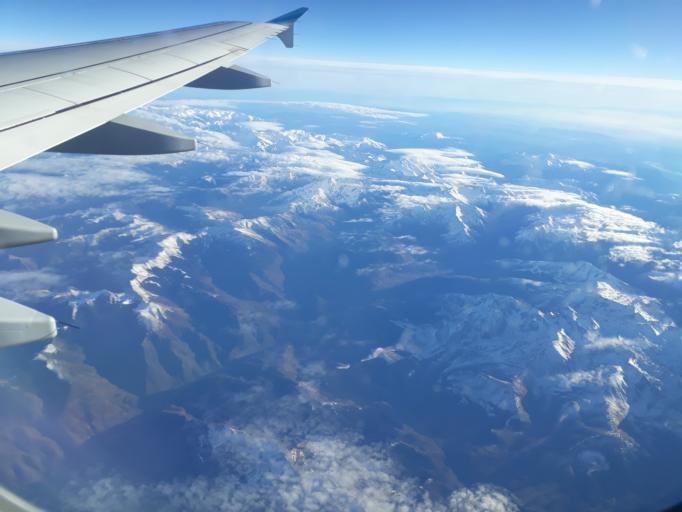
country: FR
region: Midi-Pyrenees
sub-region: Departement des Hautes-Pyrenees
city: Gerde
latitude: 43.0577
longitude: 0.2402
